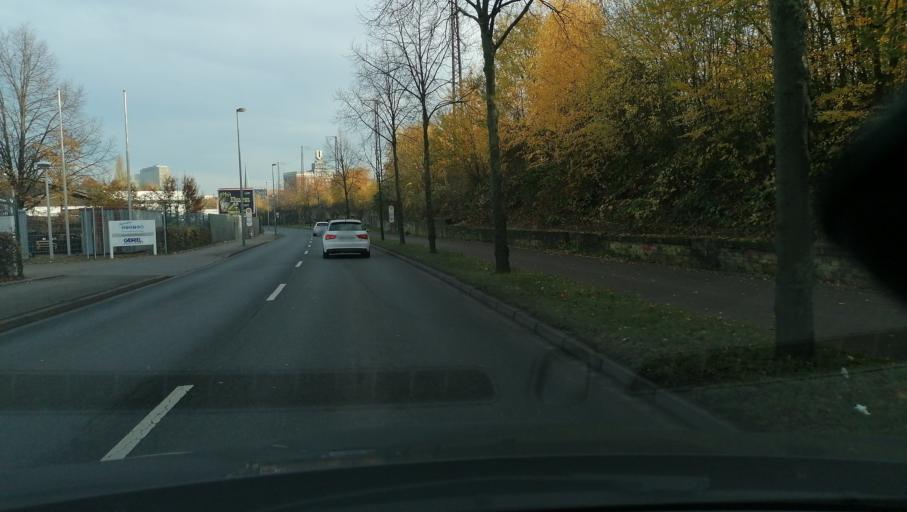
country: DE
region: North Rhine-Westphalia
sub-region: Regierungsbezirk Arnsberg
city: Dortmund
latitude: 51.5176
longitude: 7.4412
